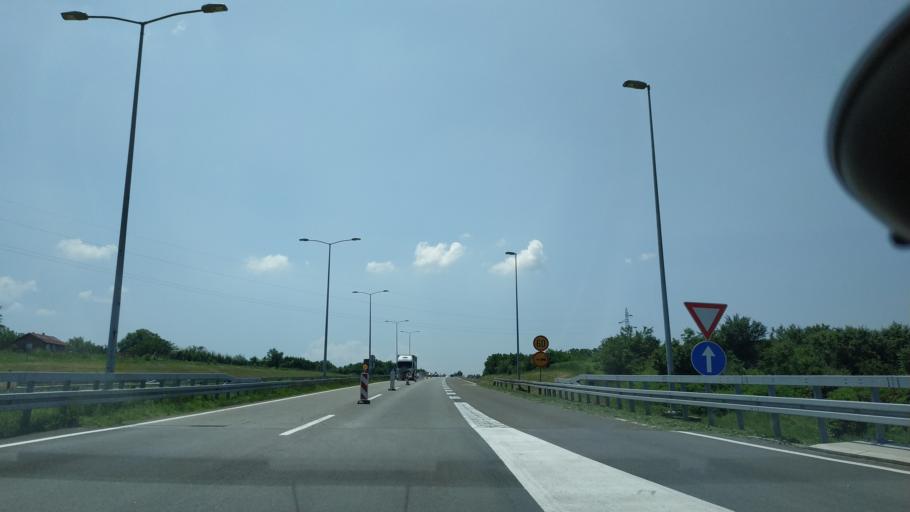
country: RS
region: Central Serbia
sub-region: Pomoravski Okrug
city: Paracin
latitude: 43.8543
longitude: 21.4348
